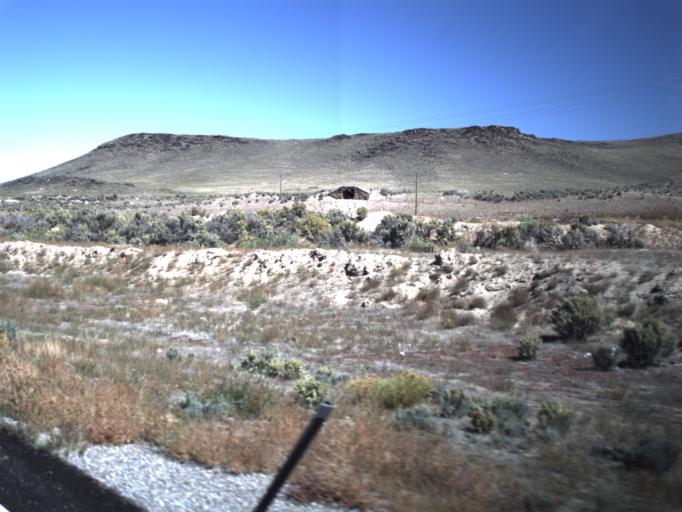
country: US
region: Utah
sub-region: Piute County
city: Junction
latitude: 38.1381
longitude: -111.9976
